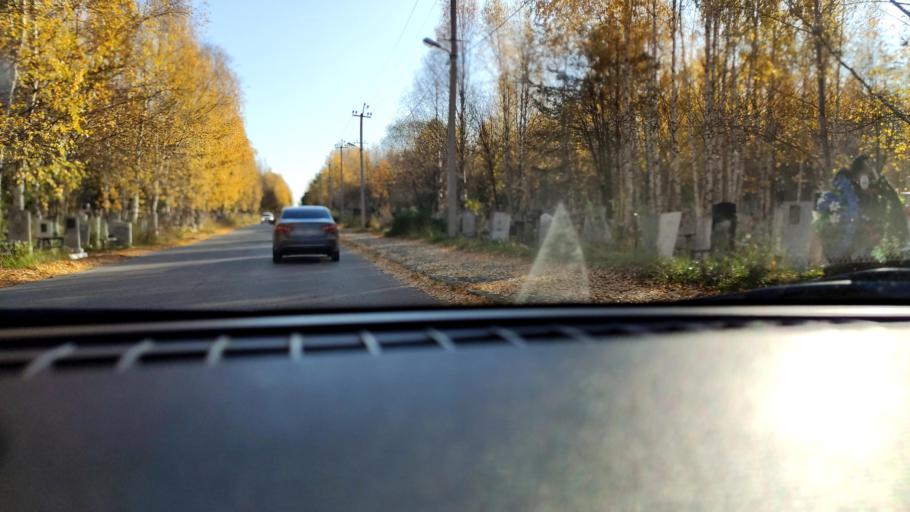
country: RU
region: Perm
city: Kondratovo
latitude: 58.0638
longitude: 56.1334
